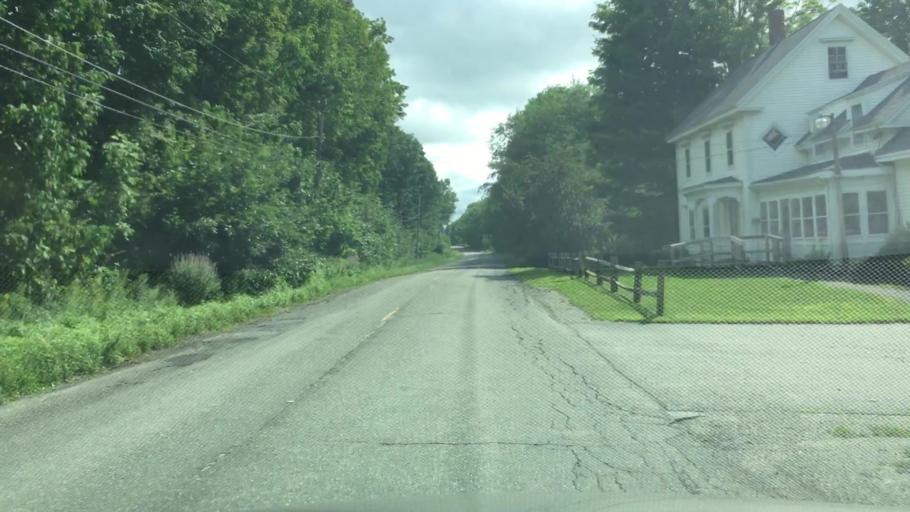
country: US
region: Maine
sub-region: Penobscot County
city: Hampden
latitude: 44.7277
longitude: -68.8629
